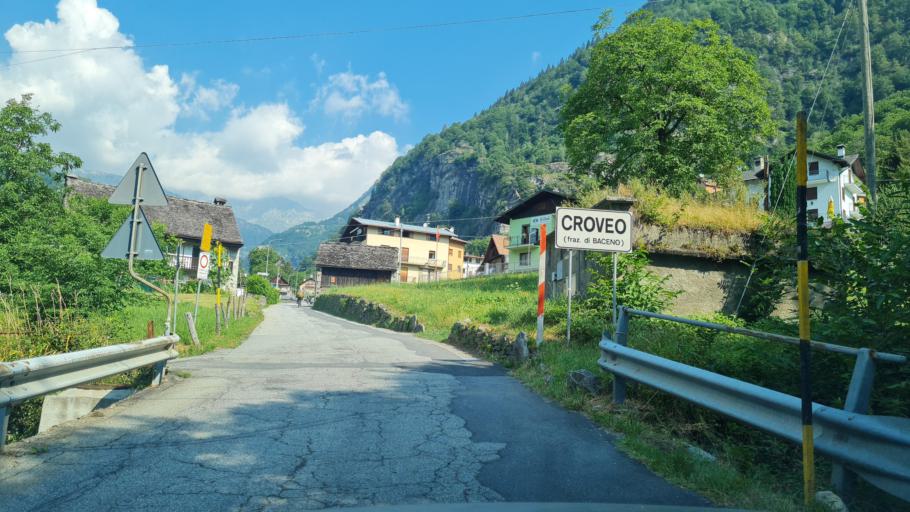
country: IT
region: Piedmont
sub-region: Provincia Verbano-Cusio-Ossola
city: Baceno
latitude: 46.2692
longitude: 8.3095
